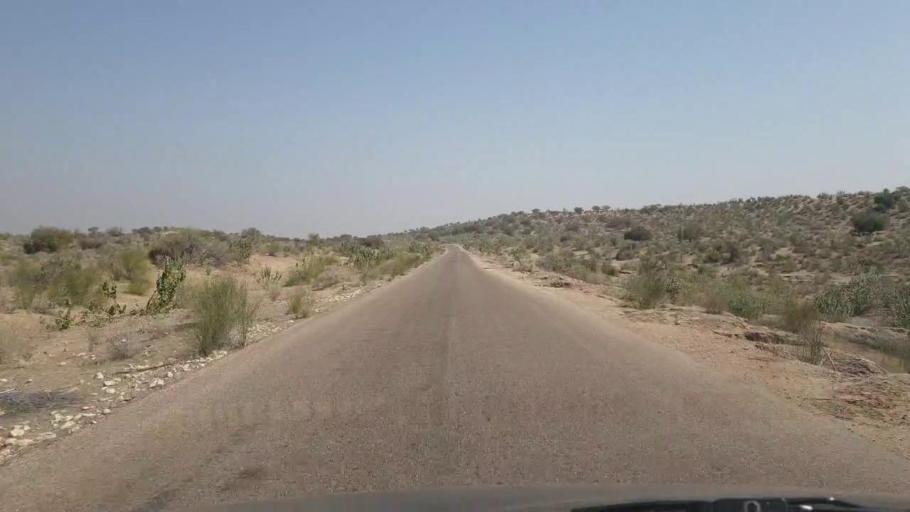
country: PK
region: Sindh
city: Chor
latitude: 25.6297
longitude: 70.0700
